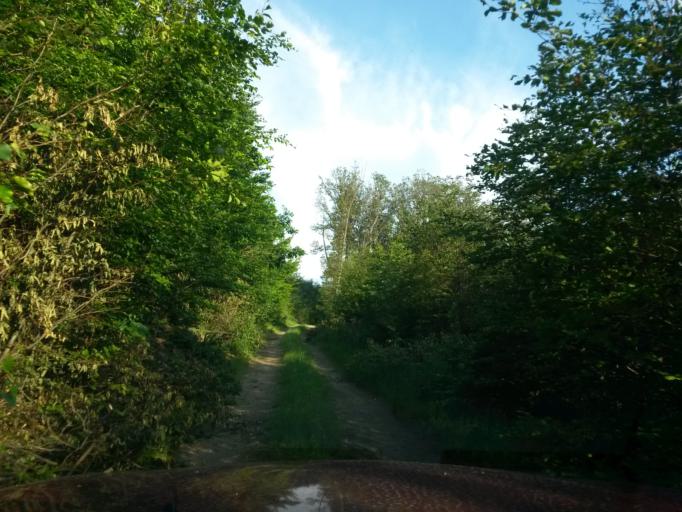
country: SK
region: Kosicky
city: Moldava nad Bodvou
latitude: 48.7370
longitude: 21.0386
